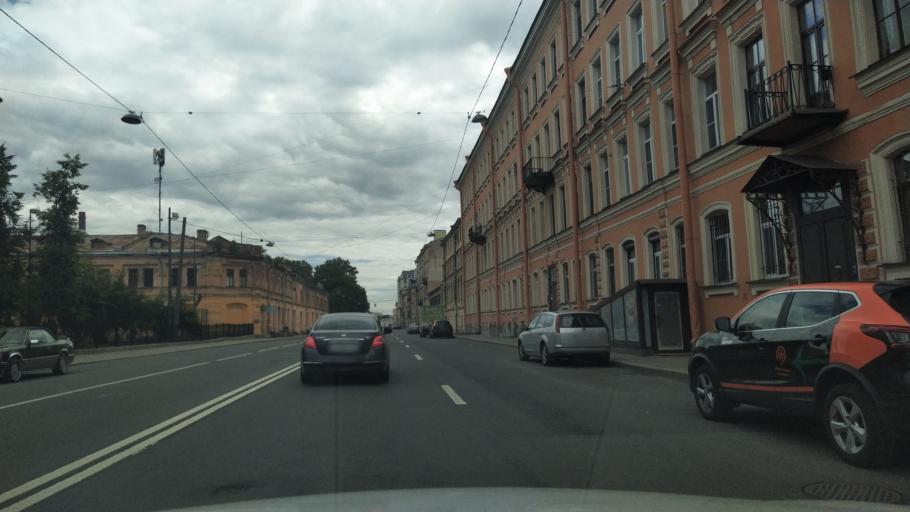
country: RU
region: St.-Petersburg
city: Centralniy
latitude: 59.9301
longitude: 30.3766
